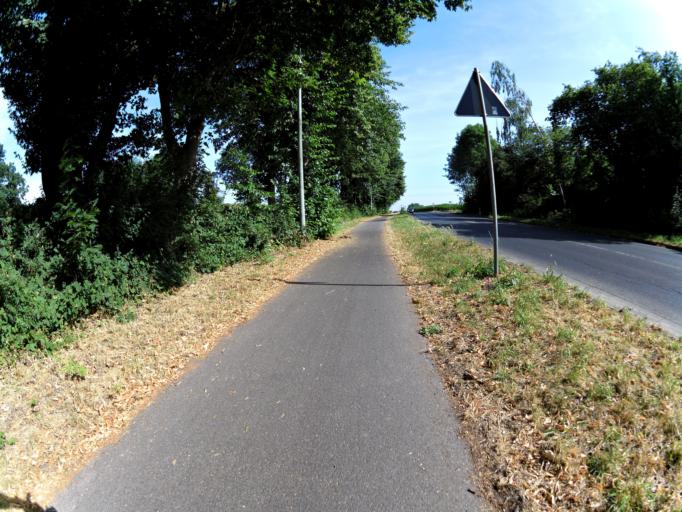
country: DE
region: North Rhine-Westphalia
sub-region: Regierungsbezirk Koln
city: Aachen
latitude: 50.8118
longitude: 6.0912
